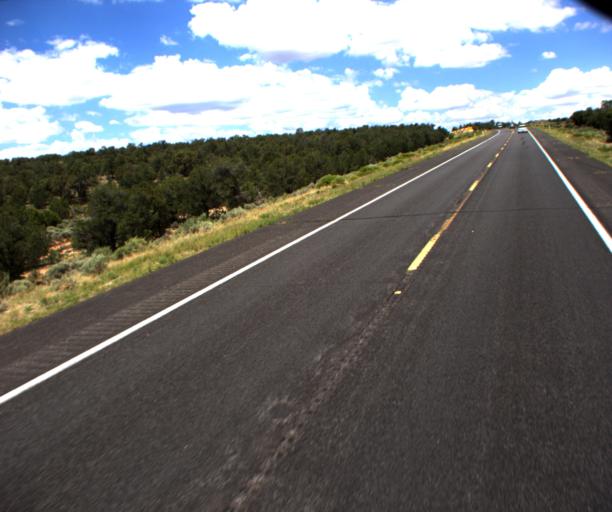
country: US
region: Arizona
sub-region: Coconino County
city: Grand Canyon
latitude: 35.9732
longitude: -111.7891
